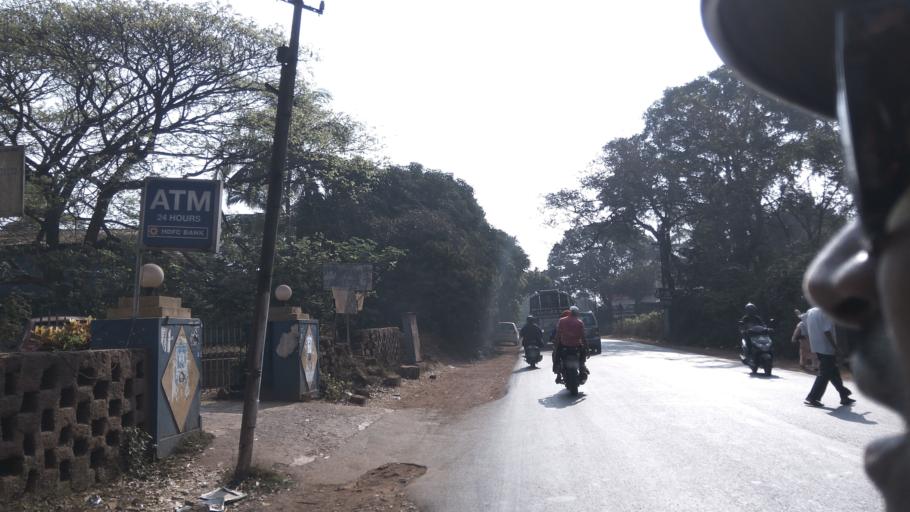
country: IN
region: Goa
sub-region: North Goa
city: Jua
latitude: 15.4960
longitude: 73.9338
